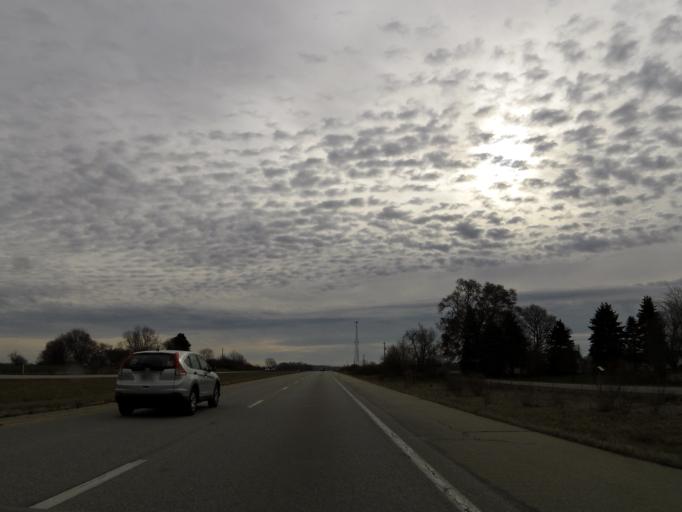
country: US
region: Indiana
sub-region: Hendricks County
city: Pittsboro
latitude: 39.9221
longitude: -86.5826
